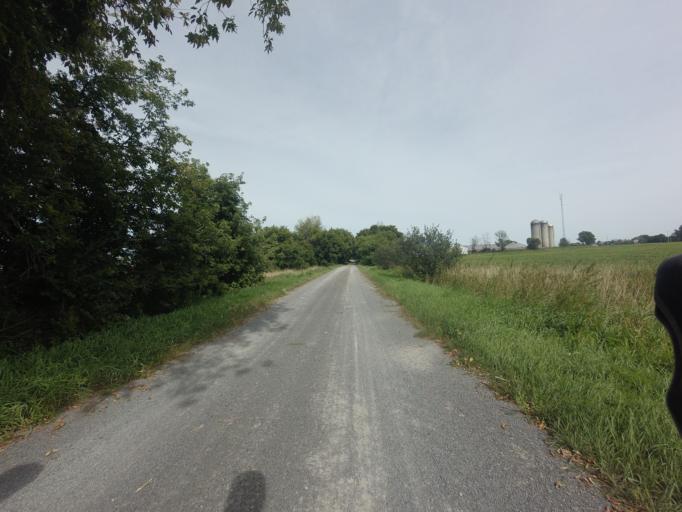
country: CA
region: Ontario
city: Carleton Place
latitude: 45.1574
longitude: -76.0871
